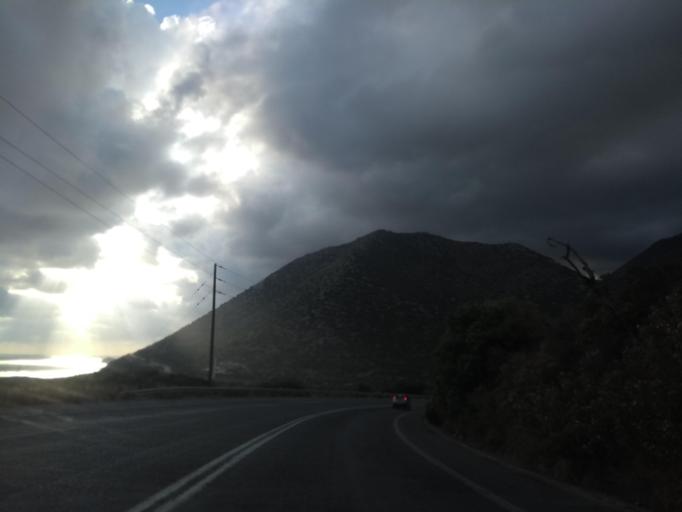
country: GR
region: Crete
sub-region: Nomos Rethymnis
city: Perama
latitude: 35.4052
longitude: 24.7790
